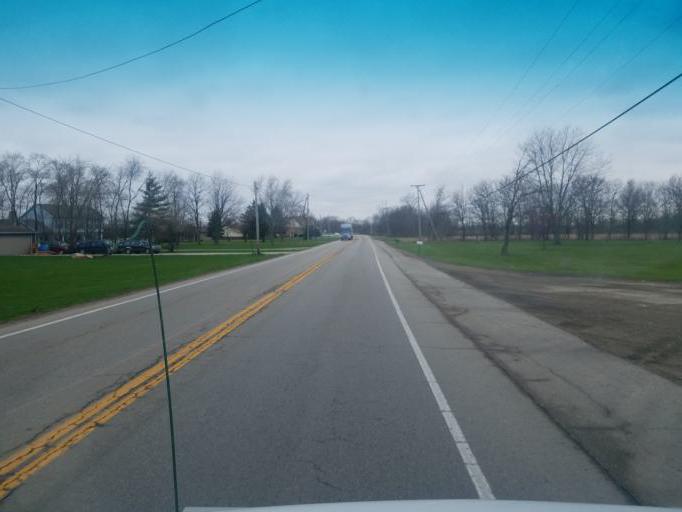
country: US
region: Ohio
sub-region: Van Wert County
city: Van Wert
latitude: 40.9003
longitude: -84.5725
